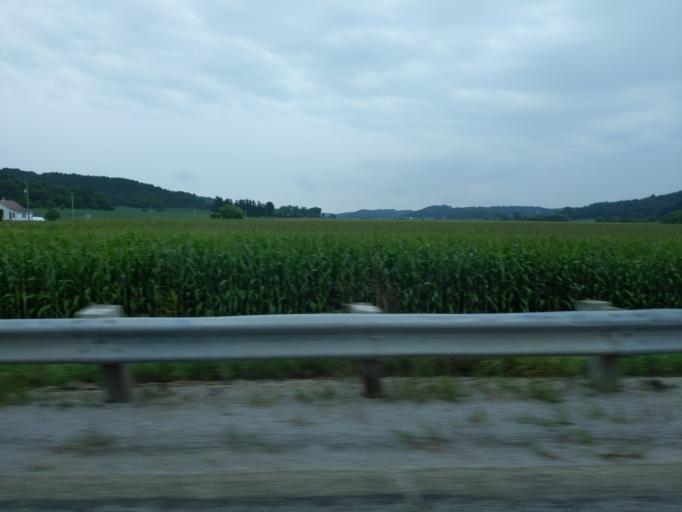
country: US
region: Wisconsin
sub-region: Dane County
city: Mazomanie
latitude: 43.1825
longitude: -89.7590
